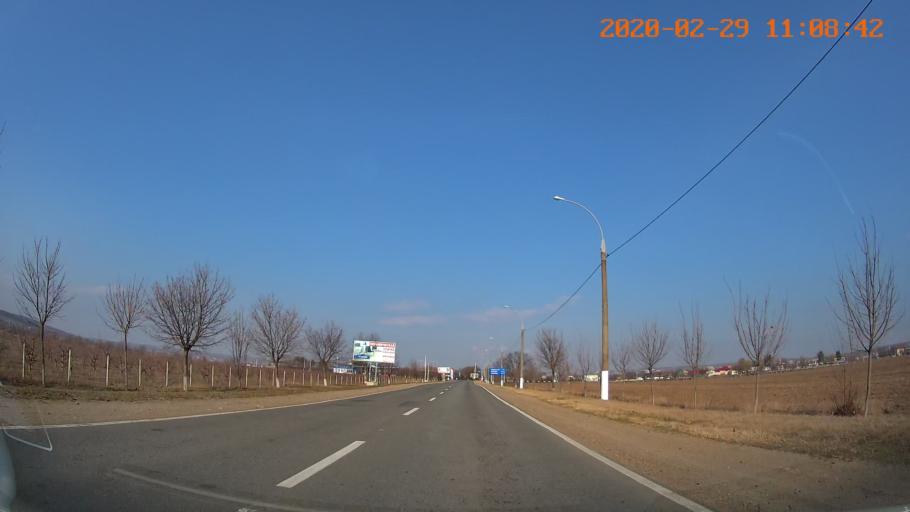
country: MD
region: Criuleni
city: Criuleni
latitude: 47.2361
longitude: 29.1738
